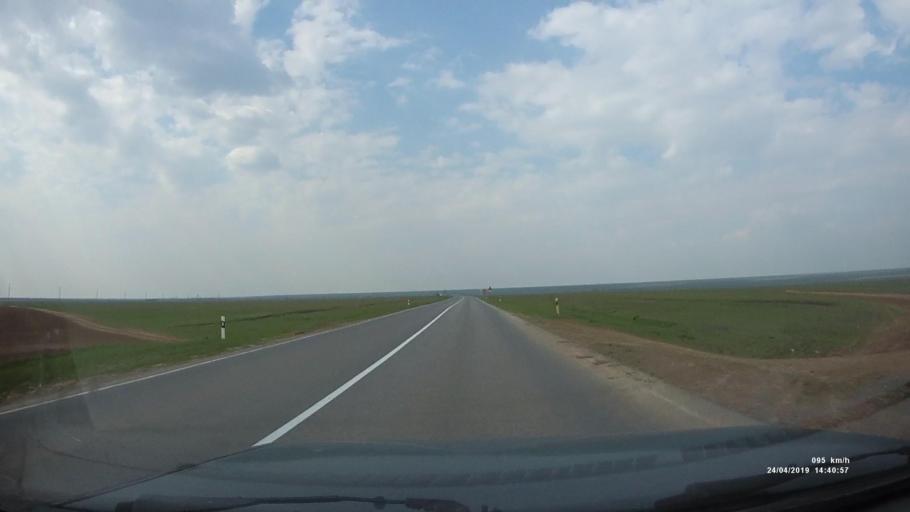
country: RU
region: Rostov
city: Remontnoye
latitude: 46.4392
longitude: 43.8845
